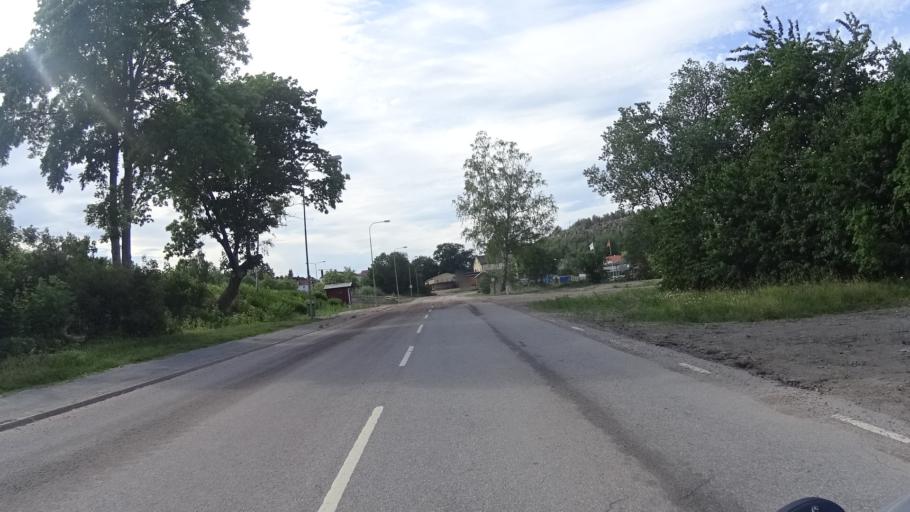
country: SE
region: Kalmar
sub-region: Vasterviks Kommun
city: Gamleby
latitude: 57.8962
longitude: 16.4120
